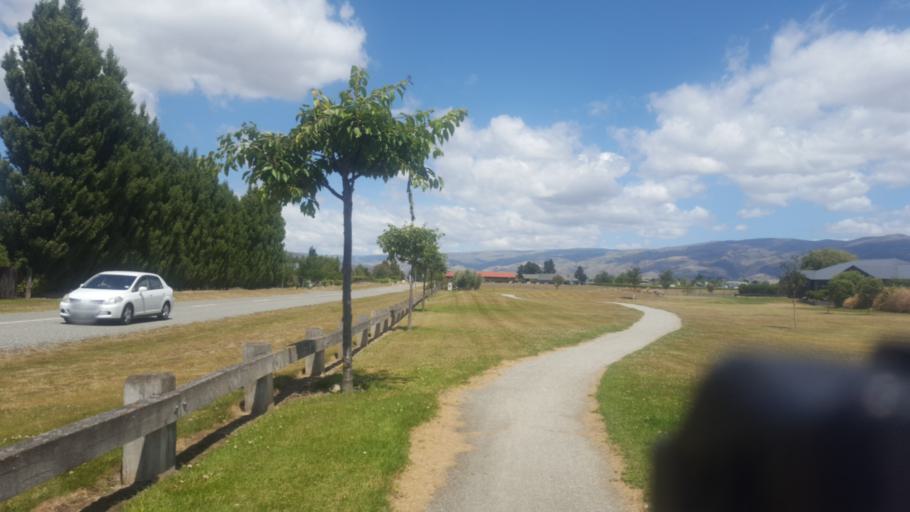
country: NZ
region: Otago
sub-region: Queenstown-Lakes District
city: Wanaka
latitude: -45.0312
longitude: 169.2033
